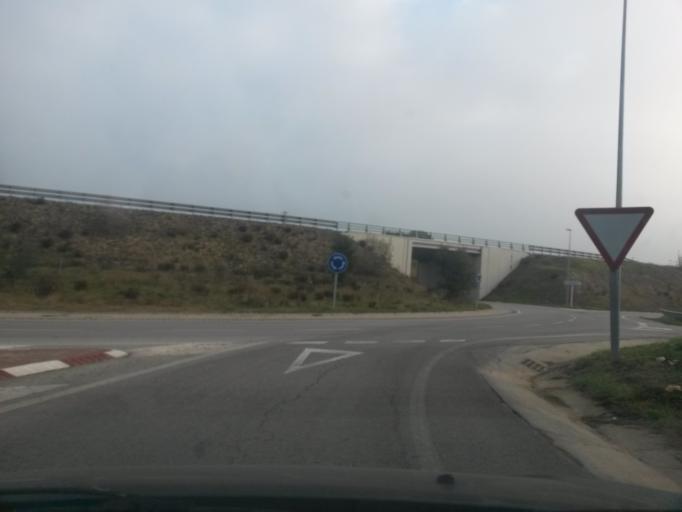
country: ES
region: Catalonia
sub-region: Provincia de Girona
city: Llagostera
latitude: 41.8299
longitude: 2.9076
